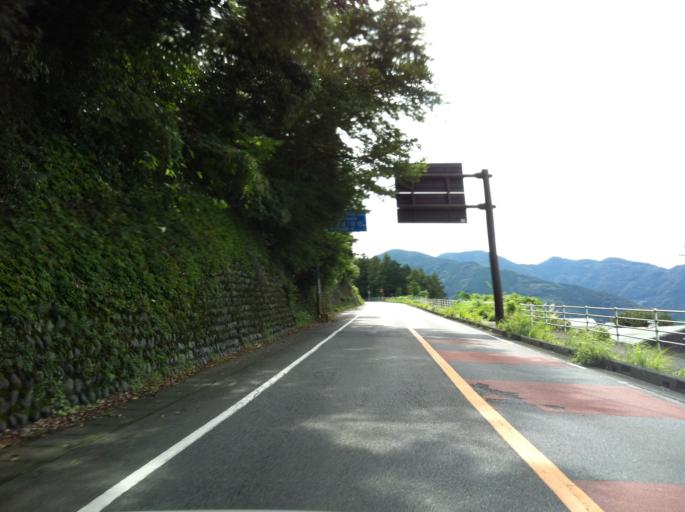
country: JP
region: Shizuoka
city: Kanaya
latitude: 34.9418
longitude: 138.0880
